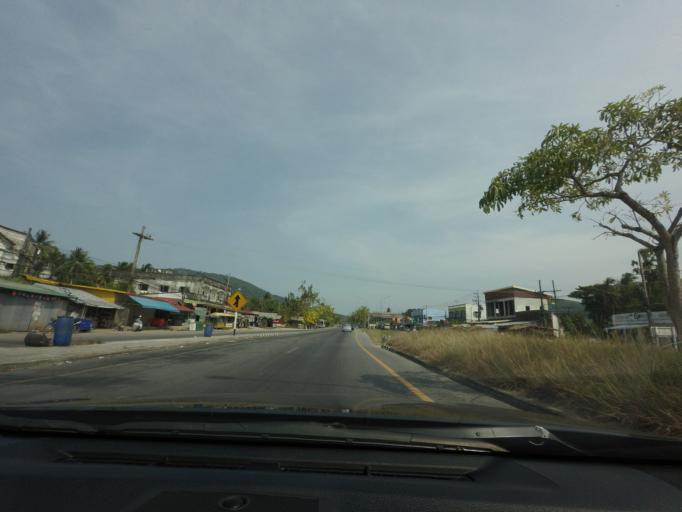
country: TH
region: Pattani
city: Mayo
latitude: 6.7548
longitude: 101.4823
